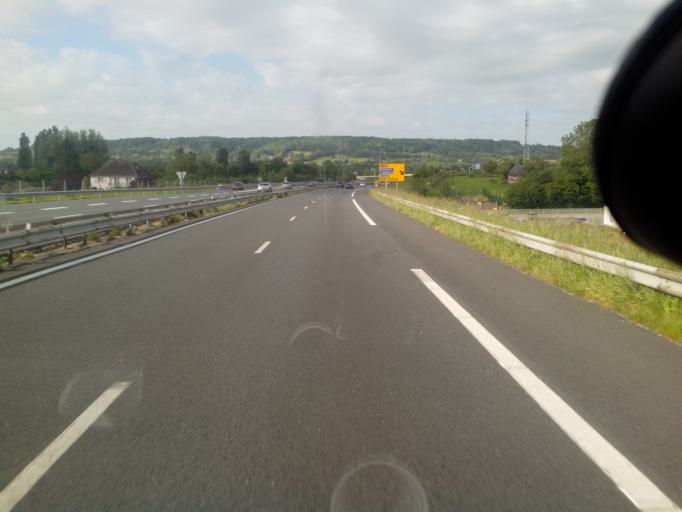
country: FR
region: Lower Normandy
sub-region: Departement du Calvados
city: Saint-Gatien-des-Bois
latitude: 49.2864
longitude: 0.1978
